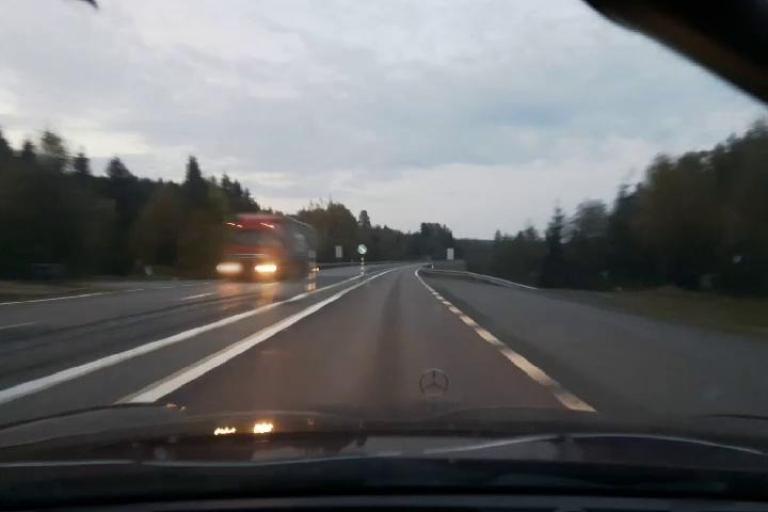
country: SE
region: Vaesternorrland
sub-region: Kramfors Kommun
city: Nordingra
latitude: 62.9557
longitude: 18.1042
